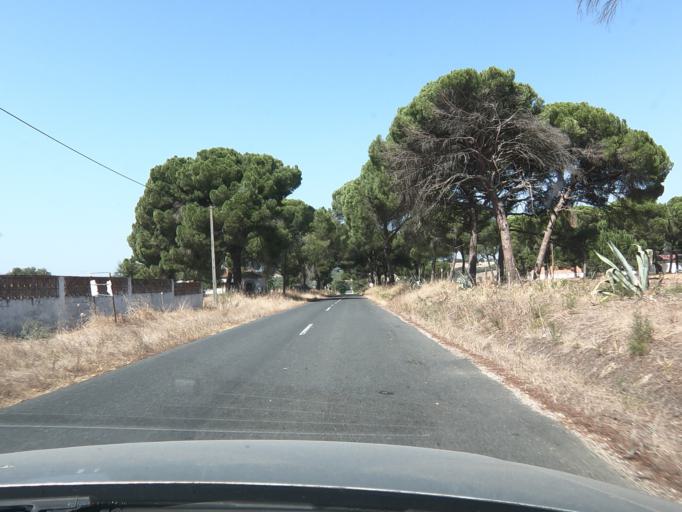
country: PT
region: Setubal
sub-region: Alcacer do Sal
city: Alcacer do Sal
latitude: 38.2815
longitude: -8.3979
